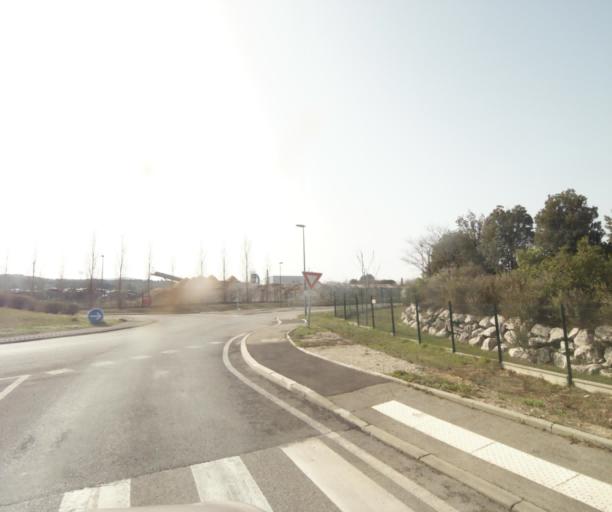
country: FR
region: Provence-Alpes-Cote d'Azur
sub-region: Departement des Bouches-du-Rhone
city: Meyreuil
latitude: 43.4689
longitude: 5.4972
